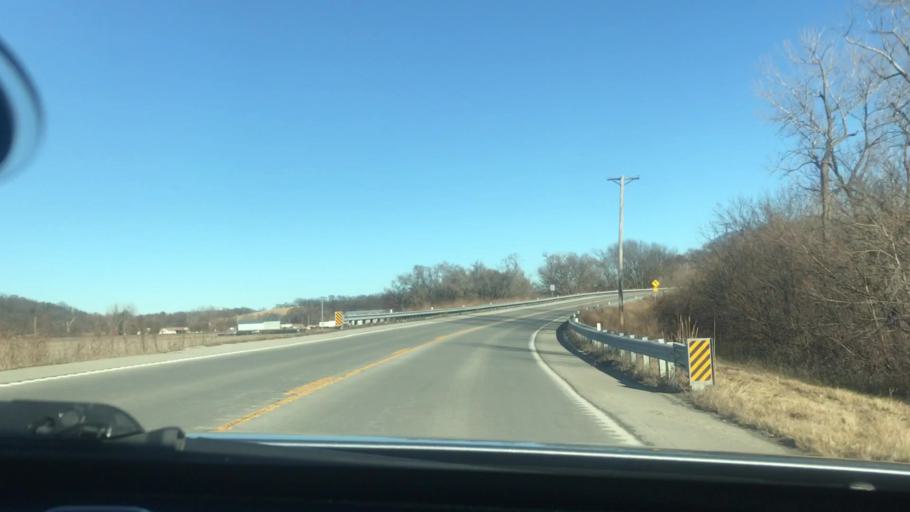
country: US
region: Missouri
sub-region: Platte County
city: Weston
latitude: 39.3639
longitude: -94.8756
